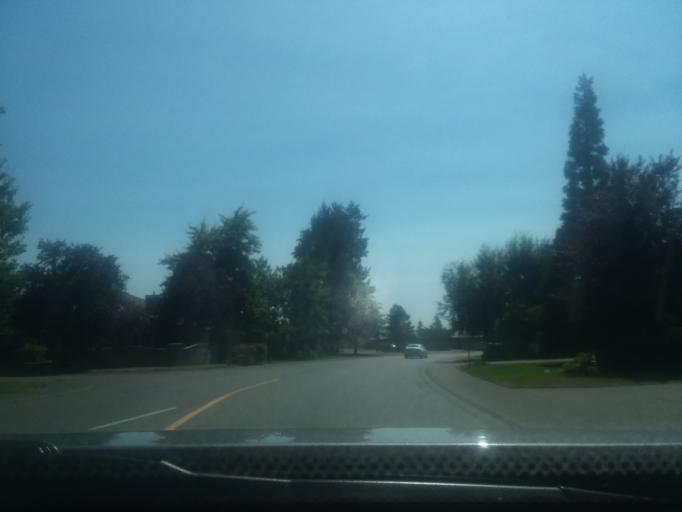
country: CA
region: British Columbia
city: Courtenay
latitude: 49.7116
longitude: -124.9599
